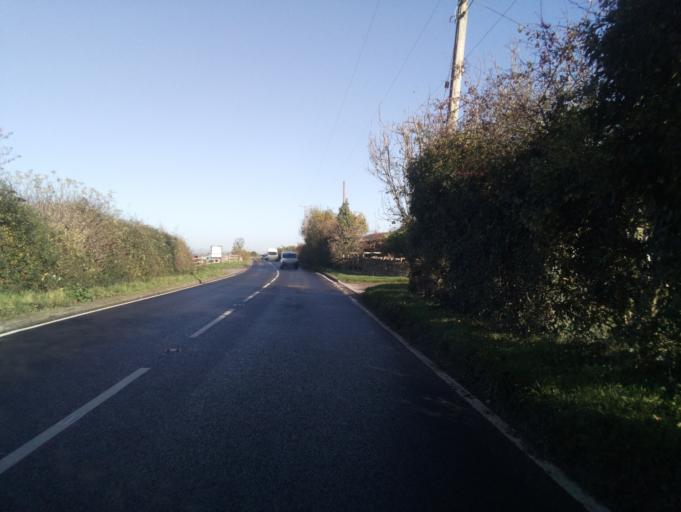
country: GB
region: England
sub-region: Somerset
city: Langport
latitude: 51.0627
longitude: -2.8578
